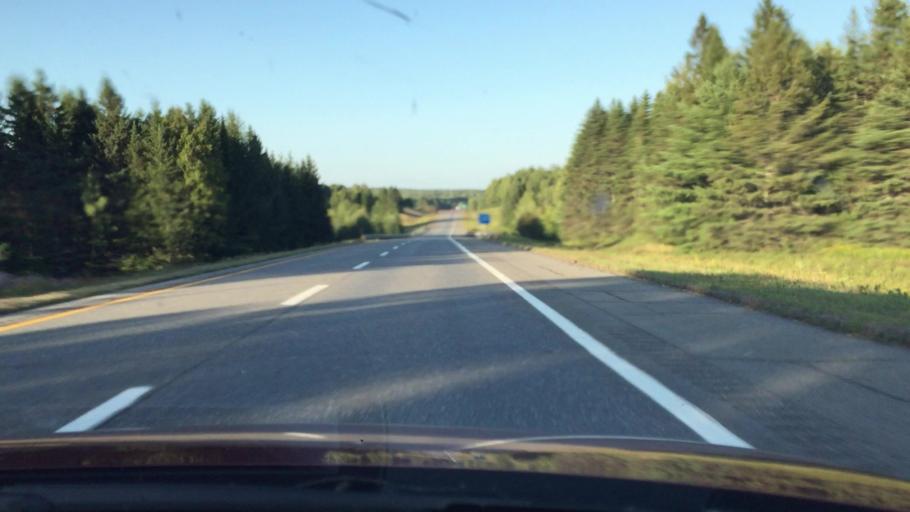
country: US
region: Maine
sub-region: Aroostook County
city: Hodgdon
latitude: 46.1365
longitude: -68.0799
